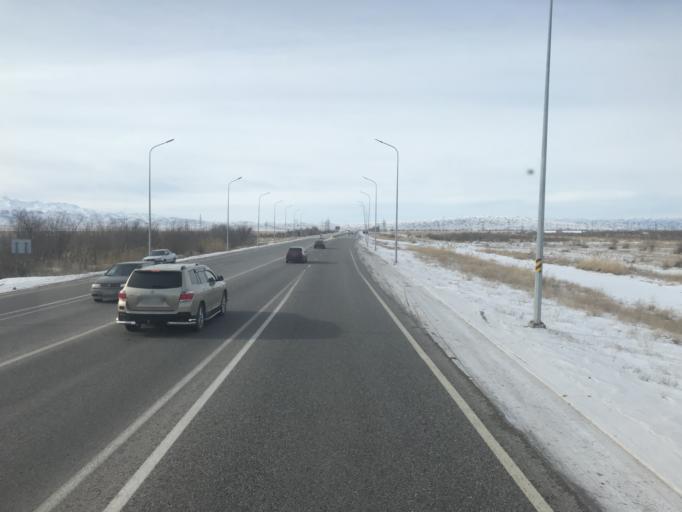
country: KZ
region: Zhambyl
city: Taraz
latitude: 42.8210
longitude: 71.1588
